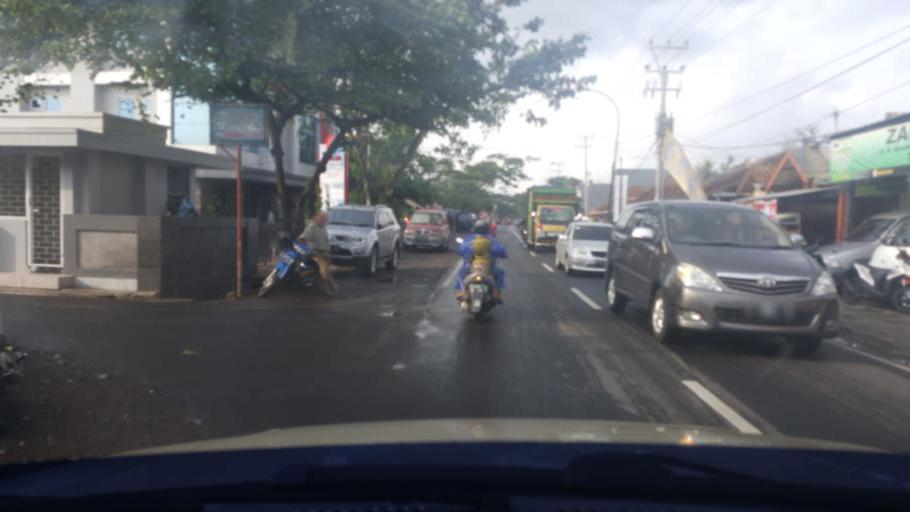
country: ID
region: West Java
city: Pakemitan
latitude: -7.2952
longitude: 108.2002
